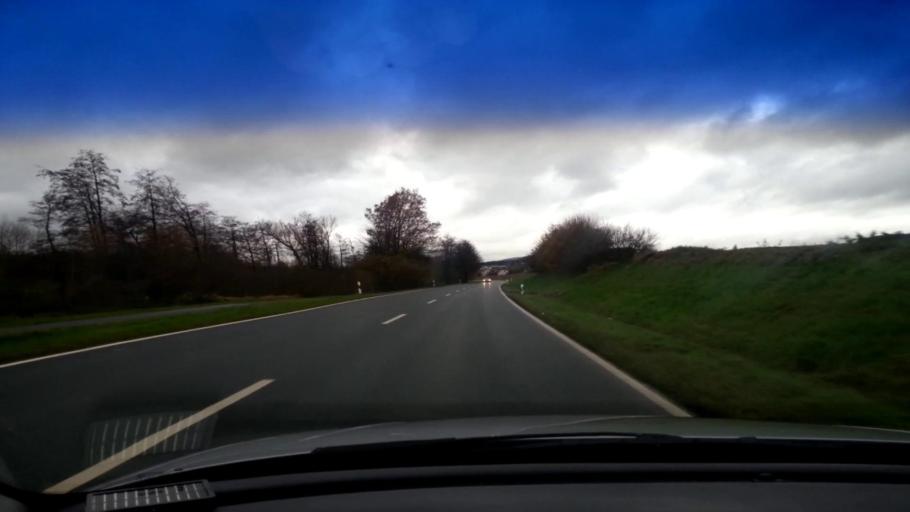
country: DE
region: Bavaria
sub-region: Upper Franconia
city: Ebensfeld
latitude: 50.0436
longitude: 10.9961
